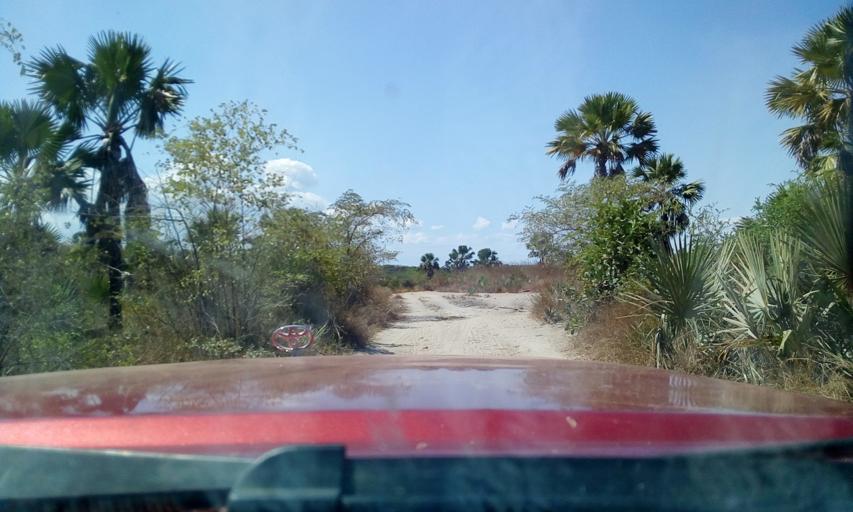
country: MG
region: Boeny
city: Sitampiky
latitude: -16.1290
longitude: 45.5036
